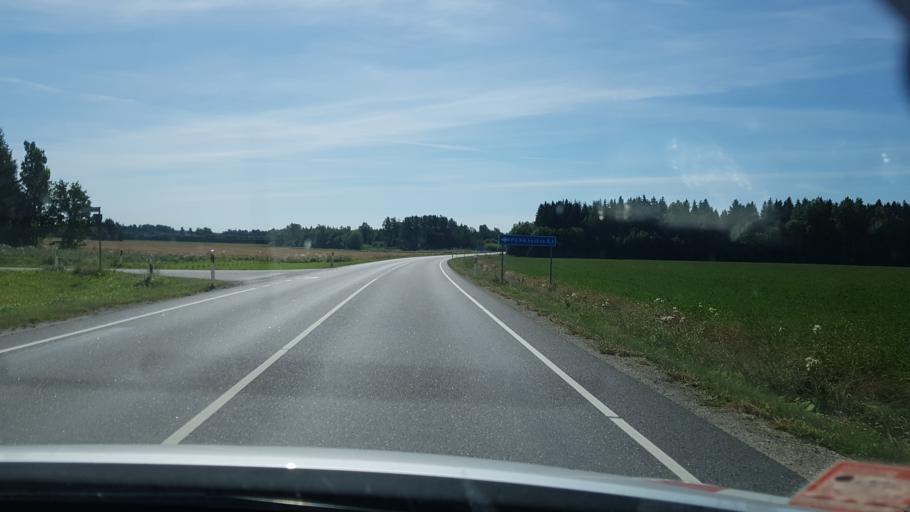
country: EE
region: Tartu
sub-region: Tartu linn
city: Tartu
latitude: 58.4089
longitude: 26.8944
